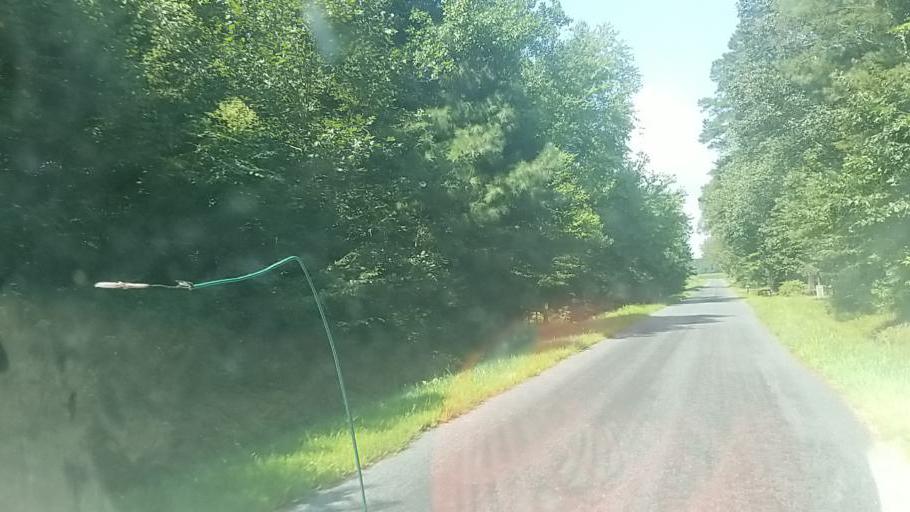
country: US
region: Maryland
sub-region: Worcester County
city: Berlin
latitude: 38.2976
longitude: -75.2868
